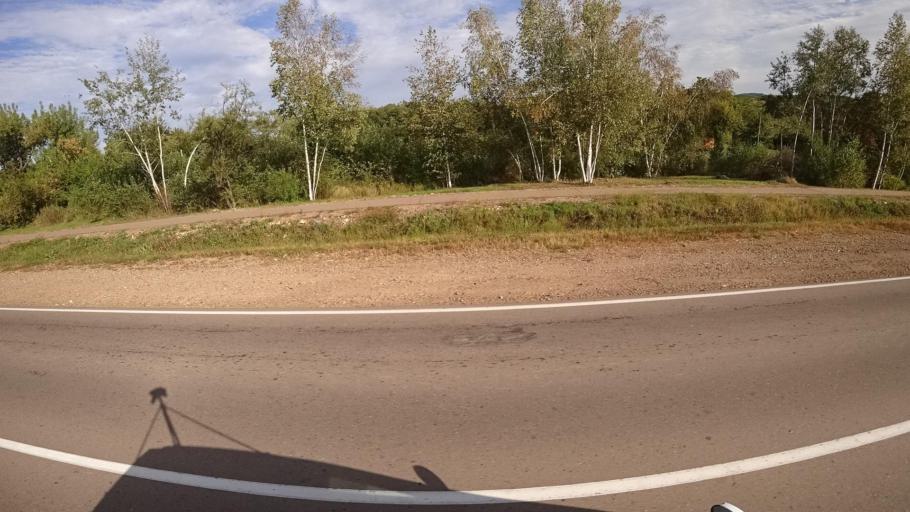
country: RU
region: Primorskiy
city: Dostoyevka
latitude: 44.2986
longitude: 133.4467
